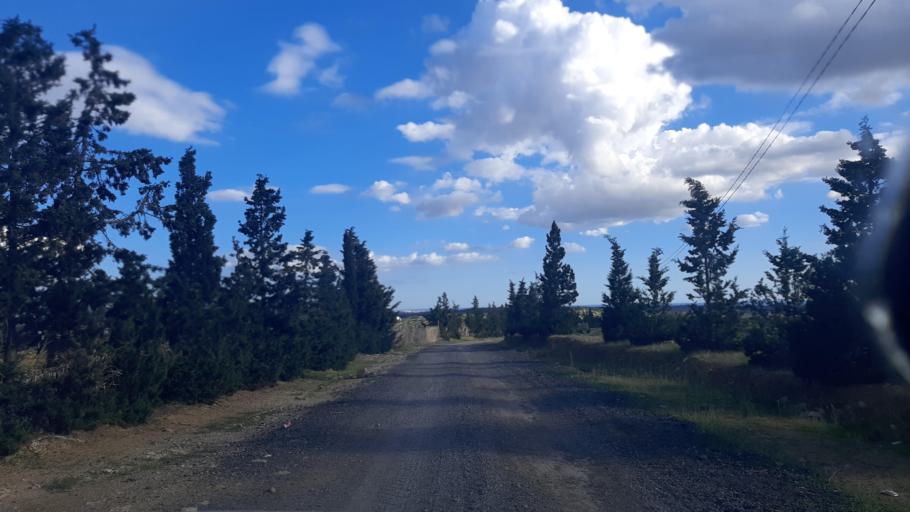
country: TN
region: Nabul
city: Bu `Urqub
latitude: 36.4694
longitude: 10.4773
